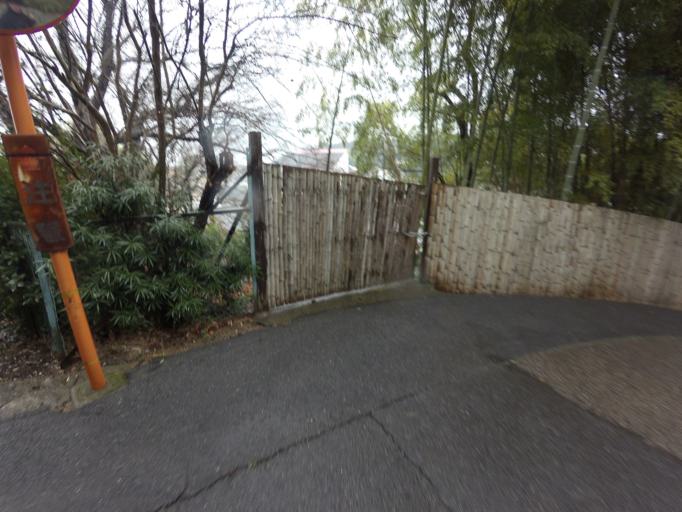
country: JP
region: Okayama
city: Kurashiki
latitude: 34.5970
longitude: 133.7745
